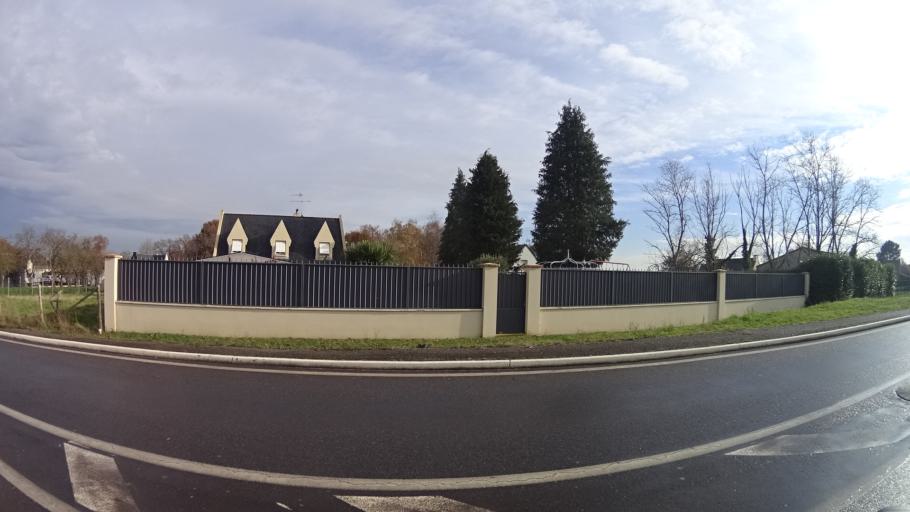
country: FR
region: Brittany
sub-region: Departement du Morbihan
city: Rieux
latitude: 47.6157
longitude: -2.1112
